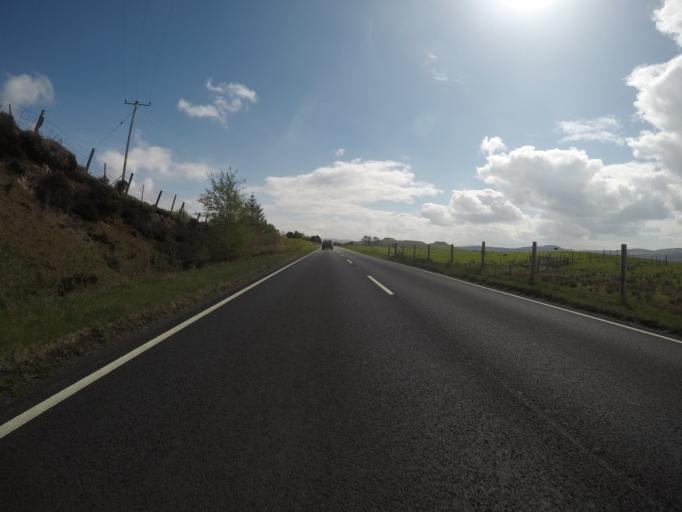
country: GB
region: Scotland
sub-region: Highland
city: Portree
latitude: 57.4955
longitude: -6.3213
